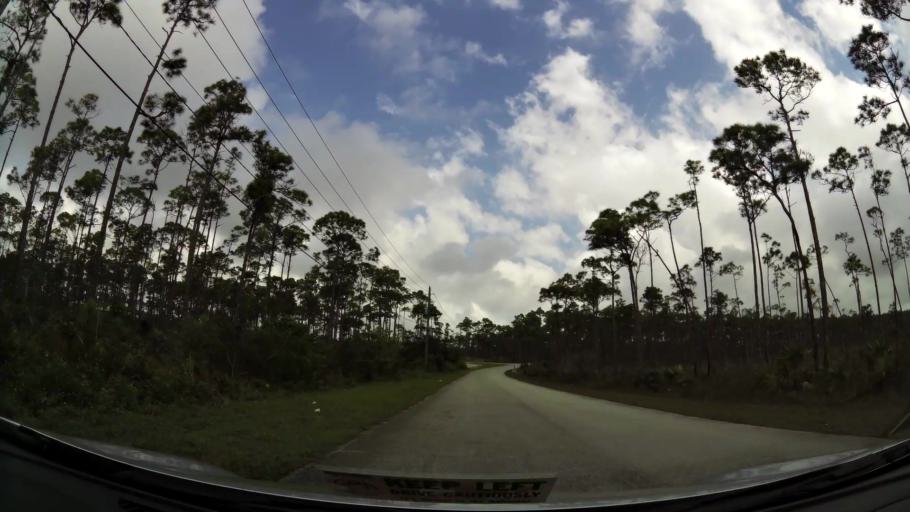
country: BS
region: Freeport
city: Lucaya
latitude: 26.5465
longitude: -78.5955
